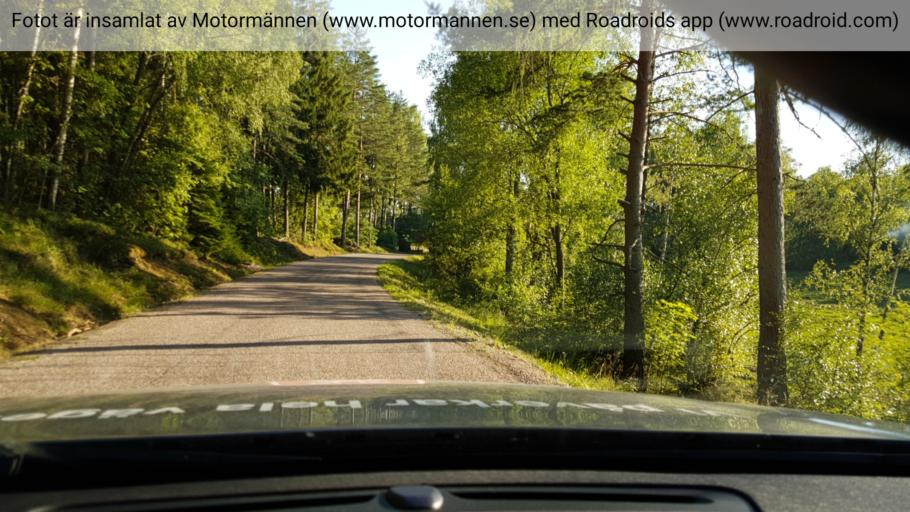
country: SE
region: Vaestmanland
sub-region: Surahammars Kommun
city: Ramnas
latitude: 59.7016
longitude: 16.0786
